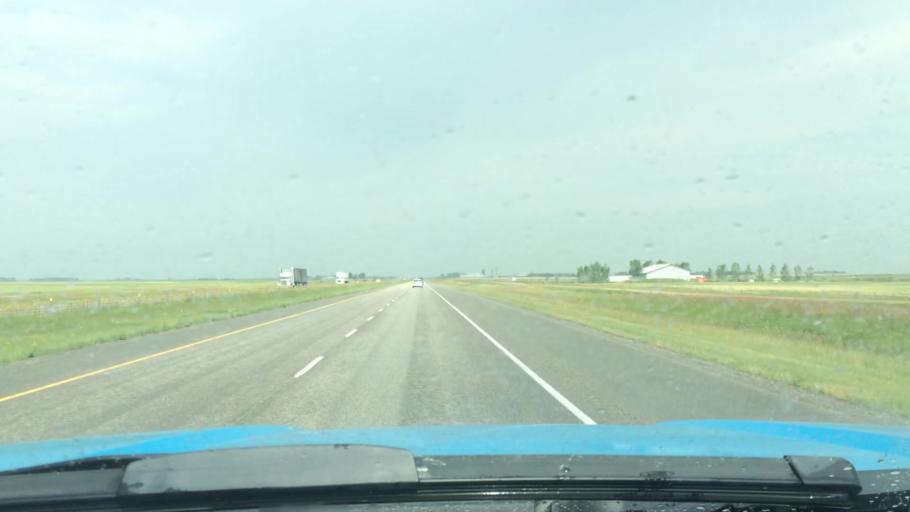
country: CA
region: Alberta
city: Didsbury
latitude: 51.6970
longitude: -114.0253
